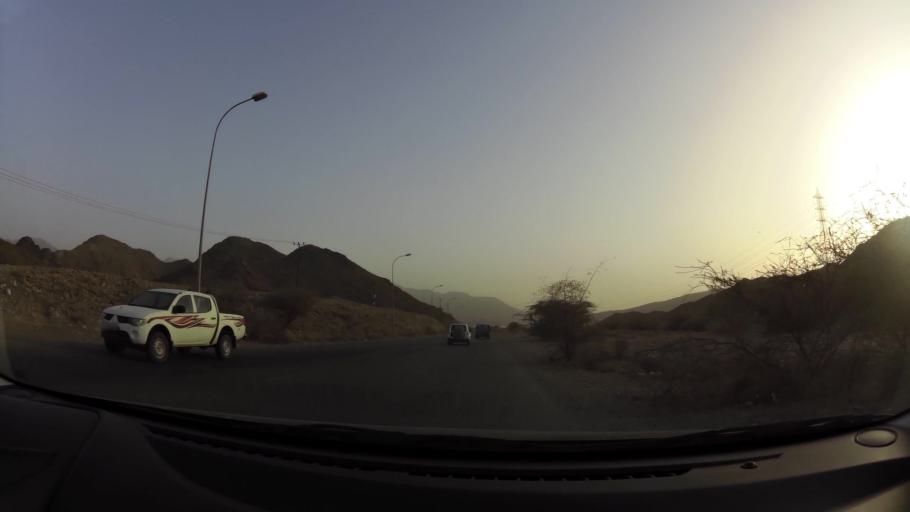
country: OM
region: Muhafazat Masqat
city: Bawshar
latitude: 23.4980
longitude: 58.3264
